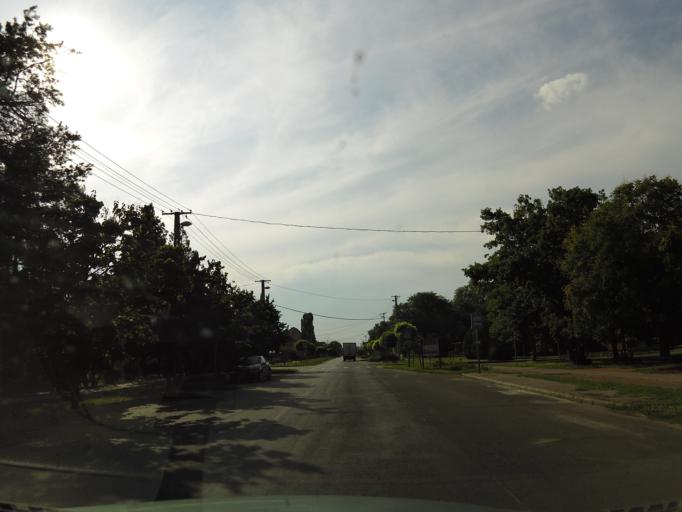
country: HU
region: Csongrad
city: Balastya
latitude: 46.4232
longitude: 20.0118
